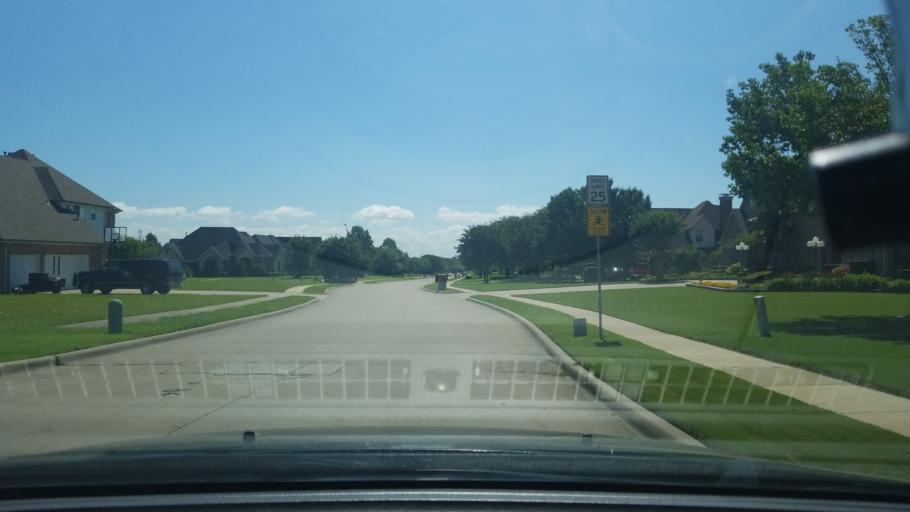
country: US
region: Texas
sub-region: Dallas County
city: Sunnyvale
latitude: 32.7896
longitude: -96.5789
